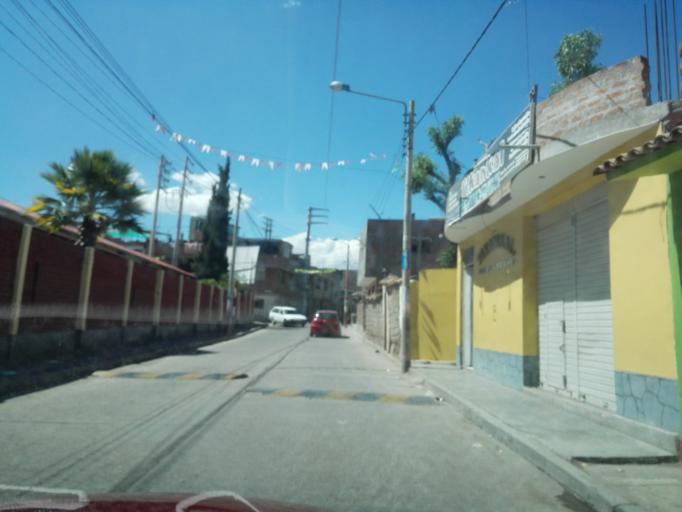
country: PE
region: Ayacucho
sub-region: Provincia de Huamanga
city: Ayacucho
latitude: -13.1574
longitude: -74.2306
